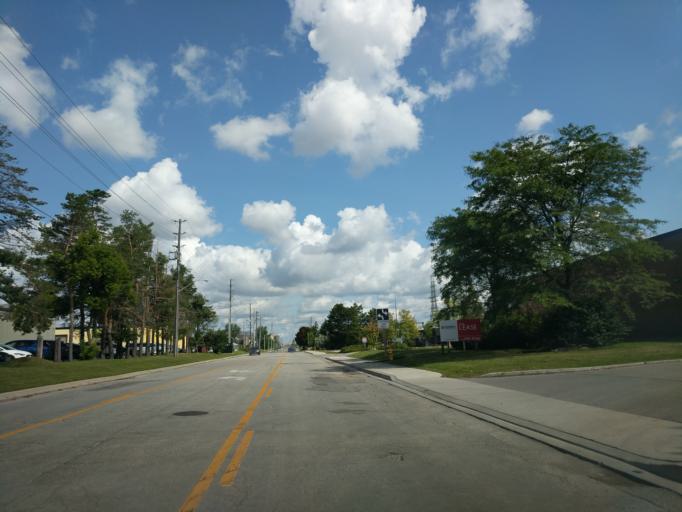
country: CA
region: Ontario
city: Scarborough
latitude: 43.8079
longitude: -79.2970
